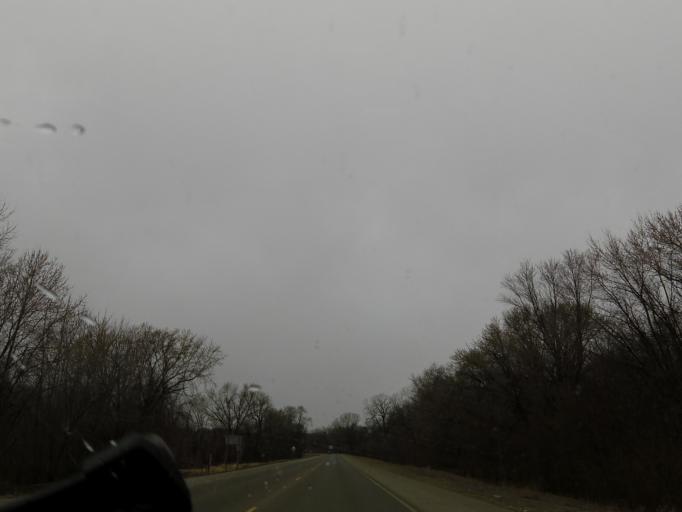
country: US
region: Minnesota
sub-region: Le Sueur County
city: Le Sueur
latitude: 44.4628
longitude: -93.9200
